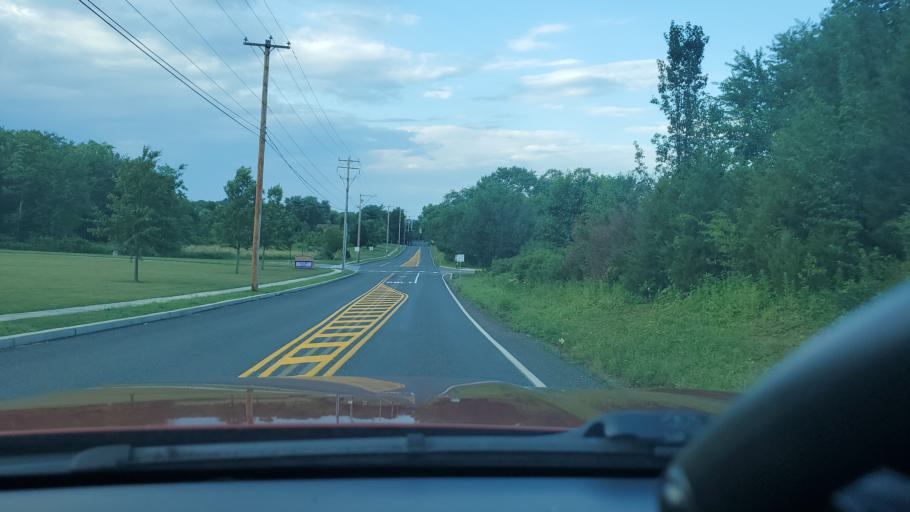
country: US
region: Pennsylvania
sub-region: Montgomery County
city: Limerick
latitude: 40.2308
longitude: -75.5100
